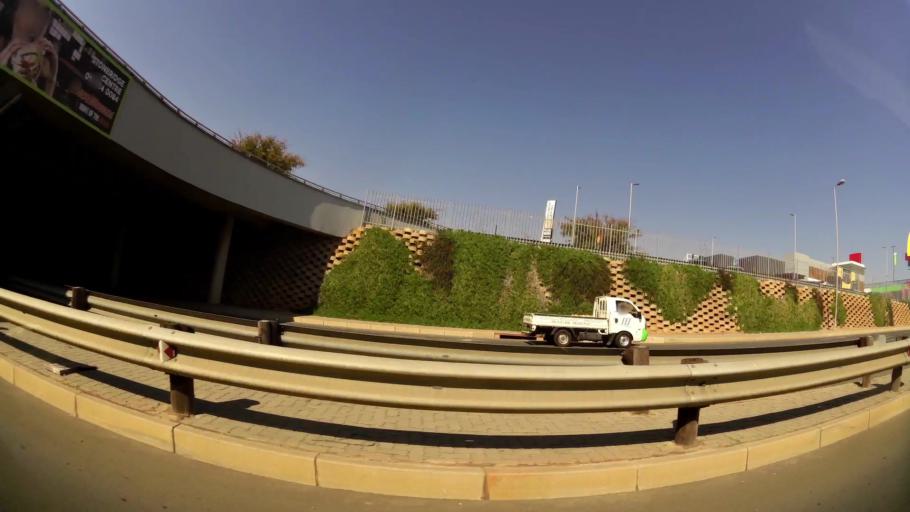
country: ZA
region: Gauteng
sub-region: City of Johannesburg Metropolitan Municipality
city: Modderfontein
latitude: -26.1170
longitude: 28.1449
